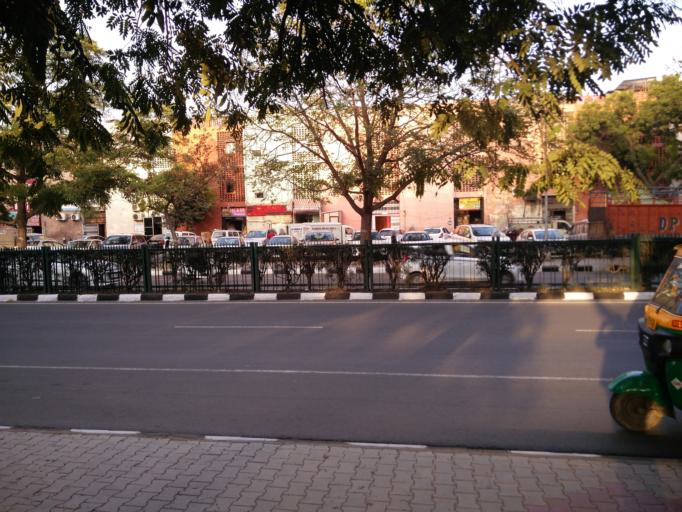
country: IN
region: Chandigarh
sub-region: Chandigarh
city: Chandigarh
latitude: 30.7216
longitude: 76.8084
